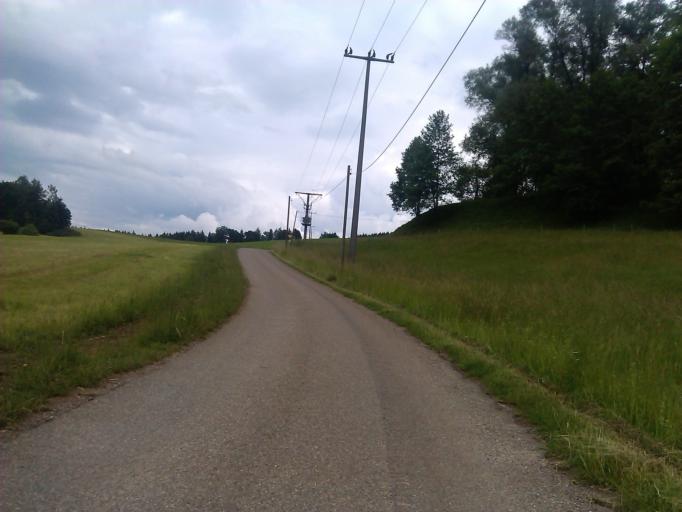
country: DE
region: Baden-Wuerttemberg
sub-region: Regierungsbezirk Stuttgart
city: Obergroningen
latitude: 48.9057
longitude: 9.9518
